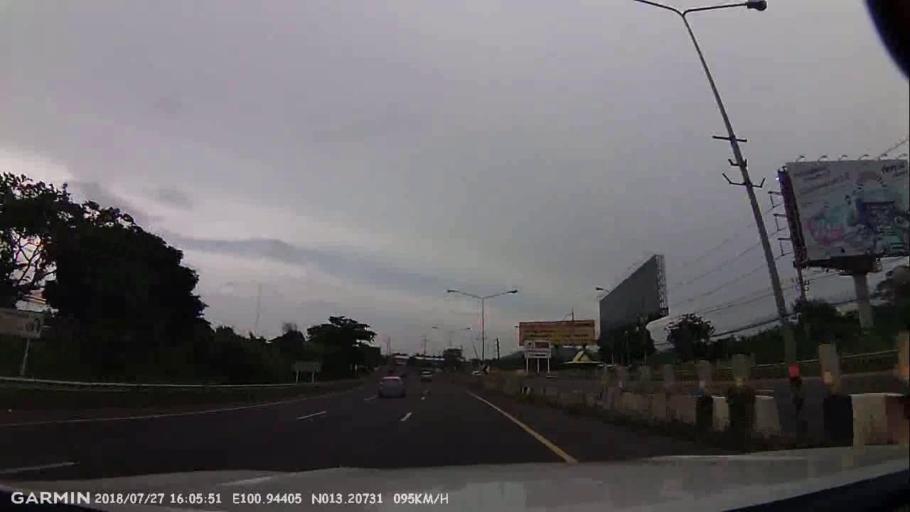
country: TH
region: Chon Buri
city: Si Racha
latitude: 13.2074
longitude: 100.9440
